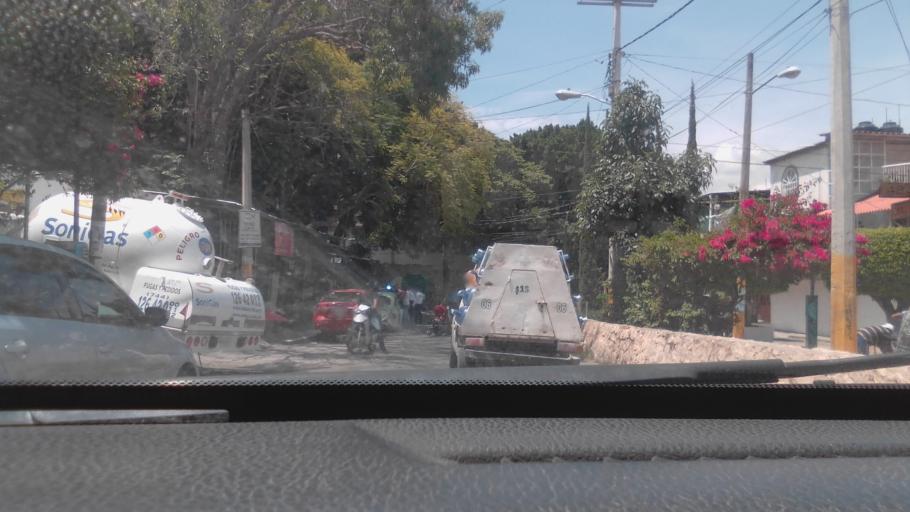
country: MX
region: Guerrero
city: Chilpancingo de los Bravos
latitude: 17.5591
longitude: -99.5047
